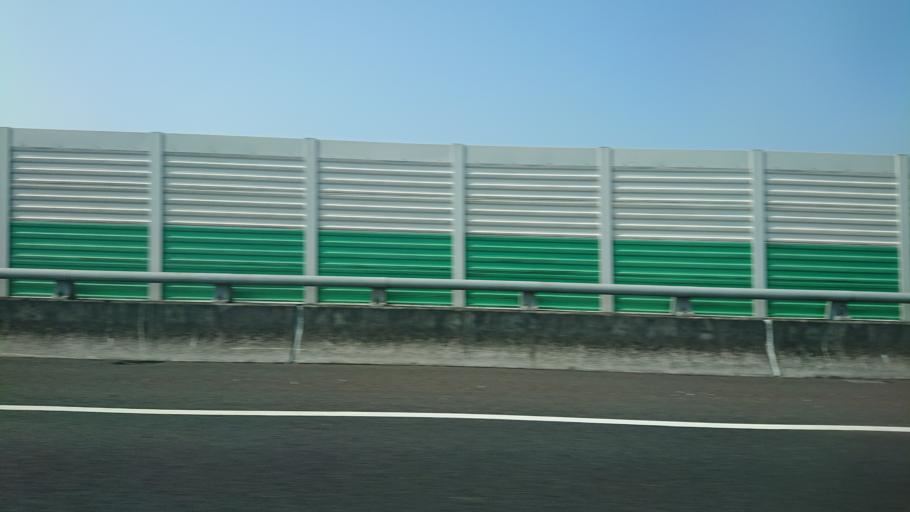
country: TW
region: Taiwan
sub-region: Nantou
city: Nantou
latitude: 23.8359
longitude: 120.7074
